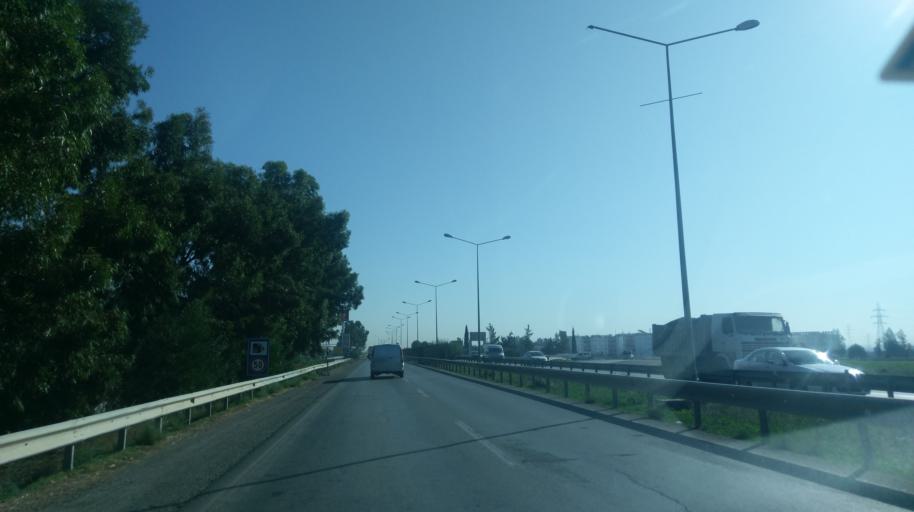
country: CY
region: Lefkosia
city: Nicosia
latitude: 35.2167
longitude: 33.4179
